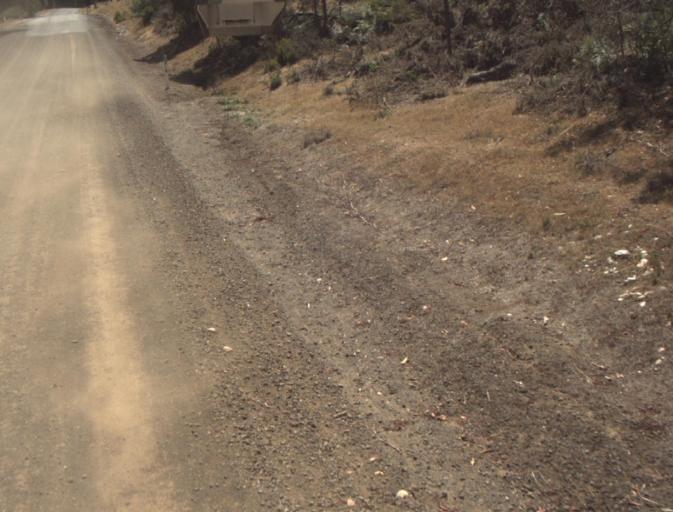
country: AU
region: Tasmania
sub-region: Launceston
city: Newstead
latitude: -41.2989
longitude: 147.3352
